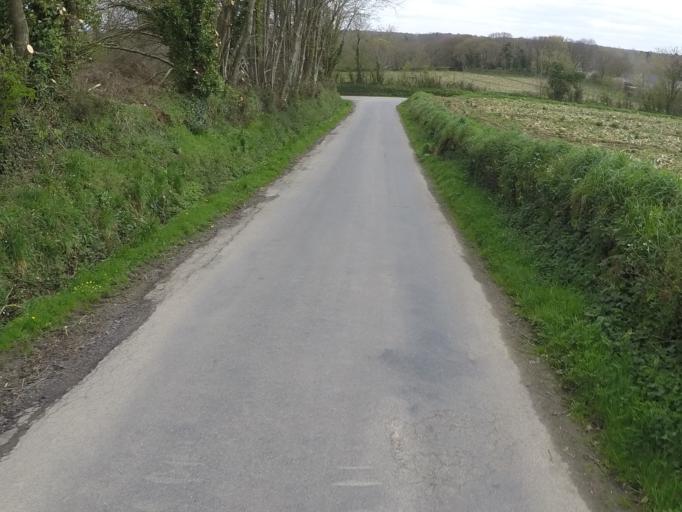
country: FR
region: Brittany
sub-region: Departement des Cotes-d'Armor
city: Plouha
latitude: 48.6735
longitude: -2.9193
